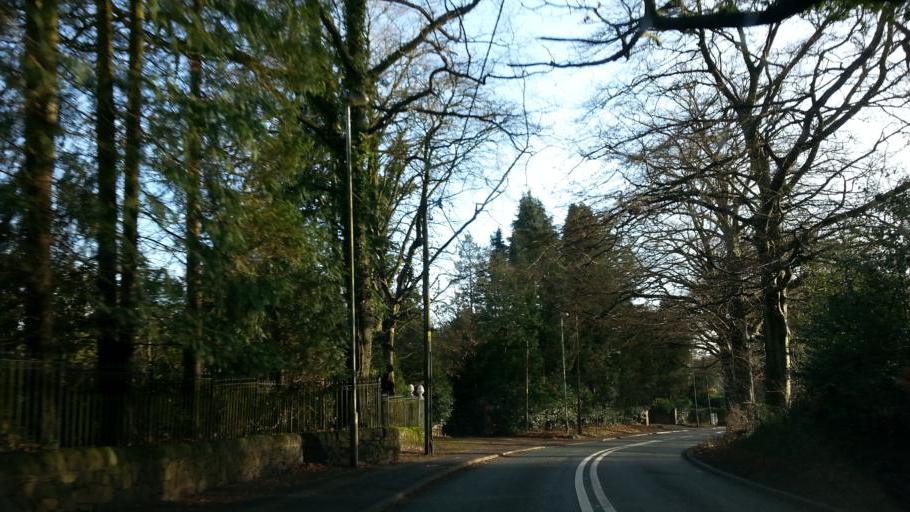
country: GB
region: England
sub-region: Staffordshire
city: Biddulph
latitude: 53.0788
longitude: -2.1205
